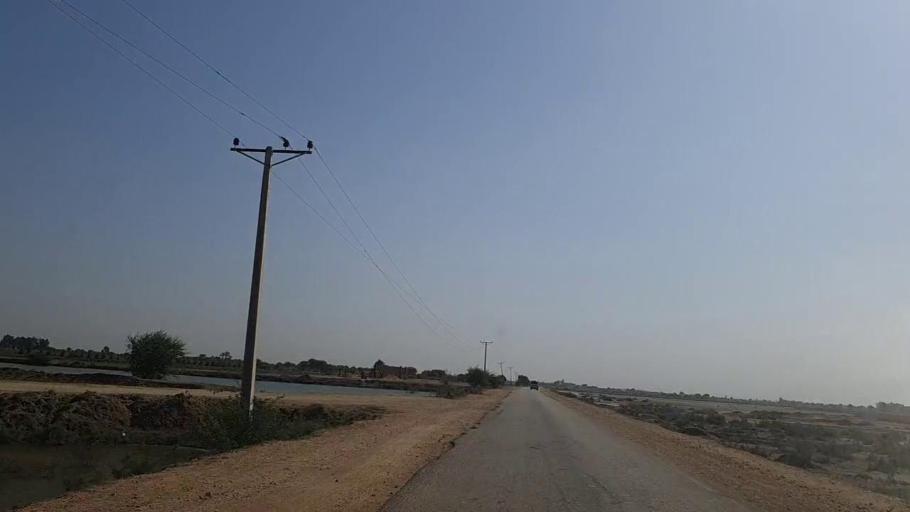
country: PK
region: Sindh
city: Mirpur Batoro
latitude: 24.6305
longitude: 68.2932
